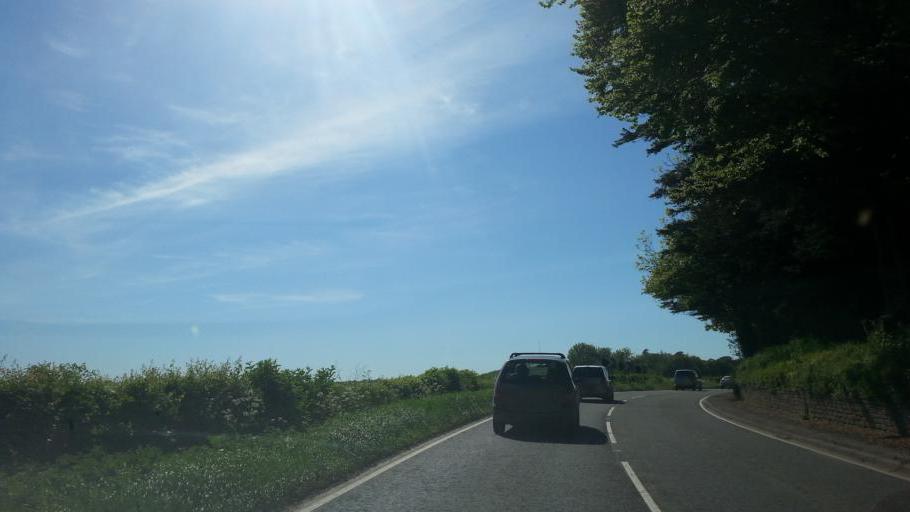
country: GB
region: England
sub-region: Somerset
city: Milborne Port
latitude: 50.9618
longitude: -2.4441
